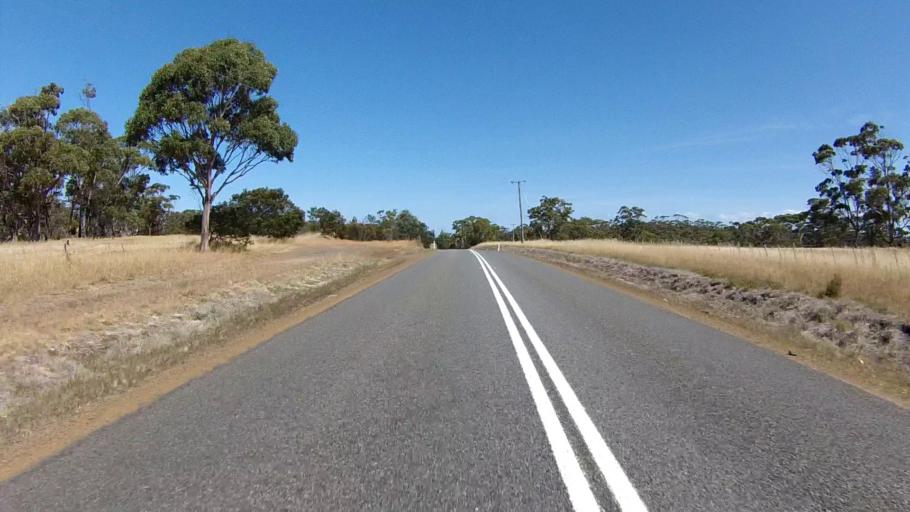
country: AU
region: Tasmania
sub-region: Sorell
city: Sorell
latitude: -42.2826
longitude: 147.9986
